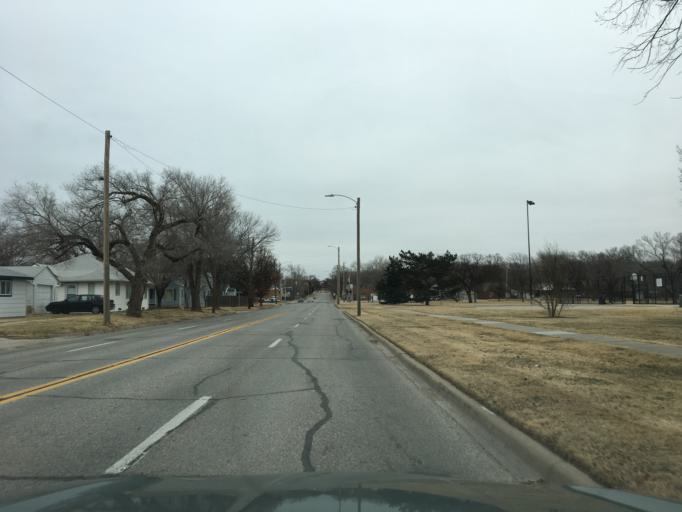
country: US
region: Kansas
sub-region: Sedgwick County
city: Wichita
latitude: 37.6718
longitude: -97.3012
